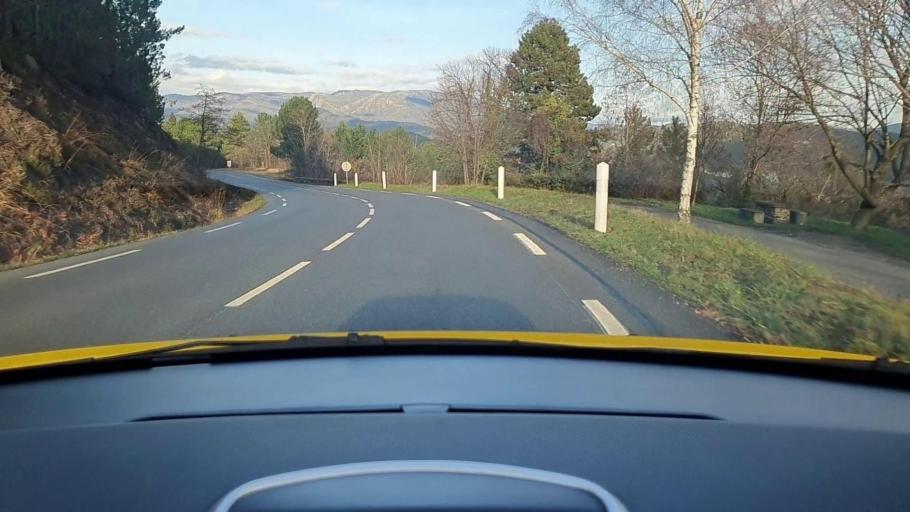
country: FR
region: Languedoc-Roussillon
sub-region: Departement du Gard
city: Branoux-les-Taillades
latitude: 44.2752
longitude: 4.0109
